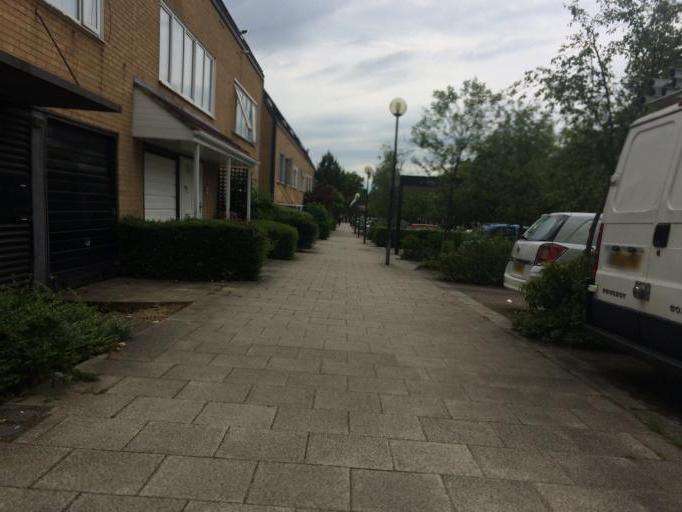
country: GB
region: England
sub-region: Milton Keynes
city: Milton Keynes
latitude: 52.0403
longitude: -0.7536
